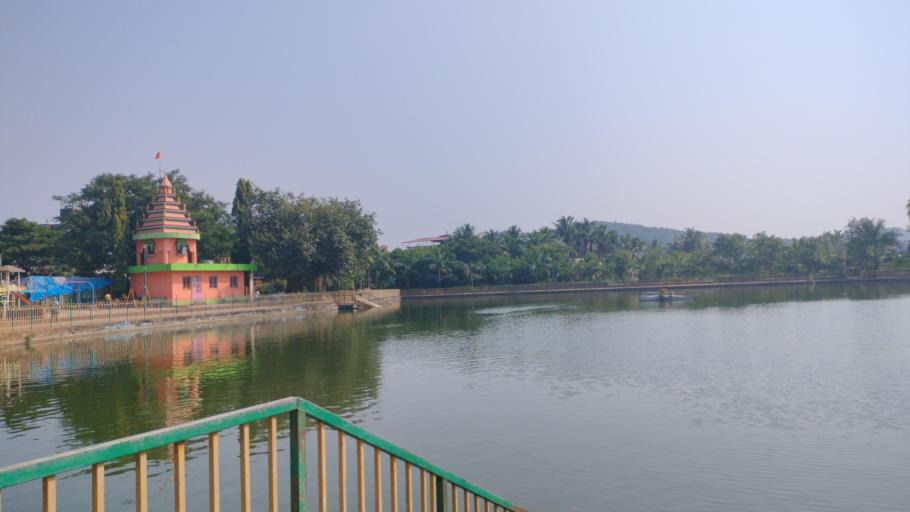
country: IN
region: Maharashtra
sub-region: Thane
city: Bhayandar
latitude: 19.3571
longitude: 72.8724
